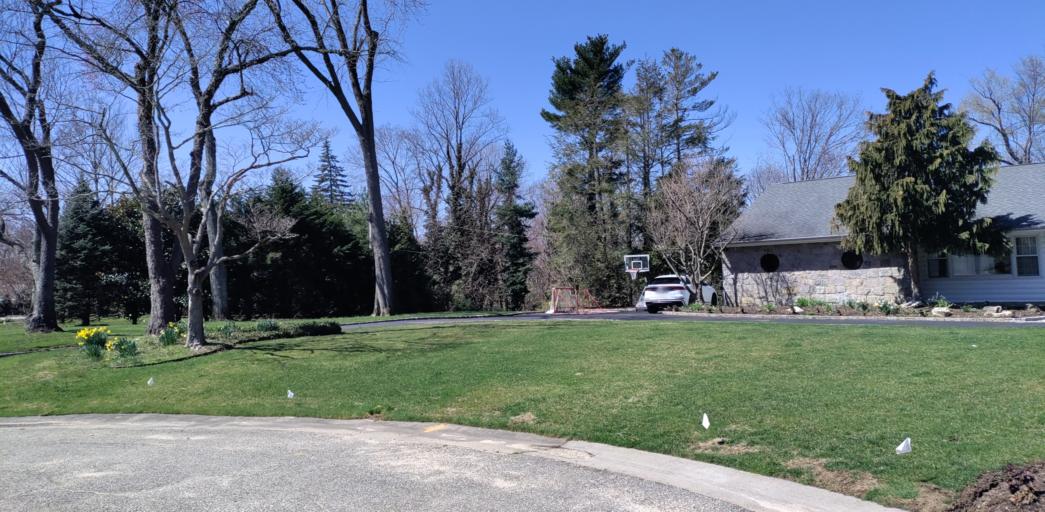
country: US
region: New York
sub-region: Nassau County
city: Roslyn Harbor
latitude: 40.8202
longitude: -73.6350
